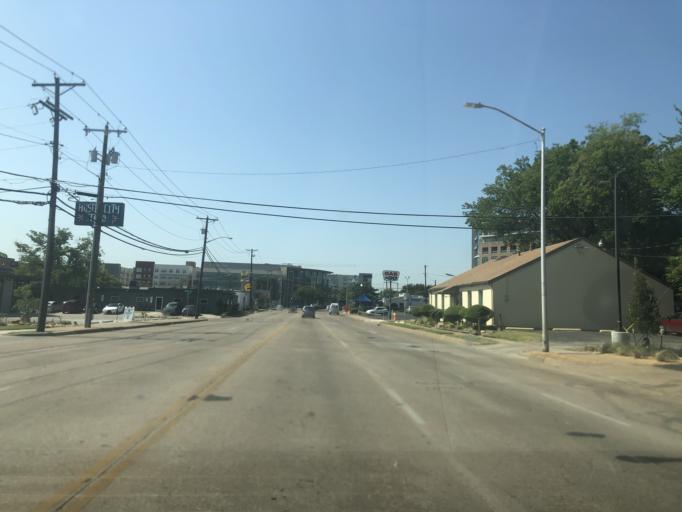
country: US
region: Texas
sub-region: Tarrant County
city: River Oaks
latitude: 32.7538
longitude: -97.3613
